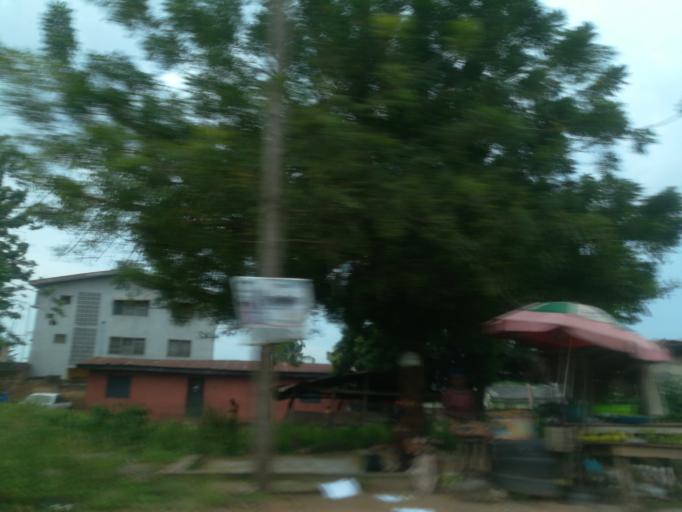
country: NG
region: Oyo
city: Moniya
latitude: 7.4547
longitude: 3.9127
